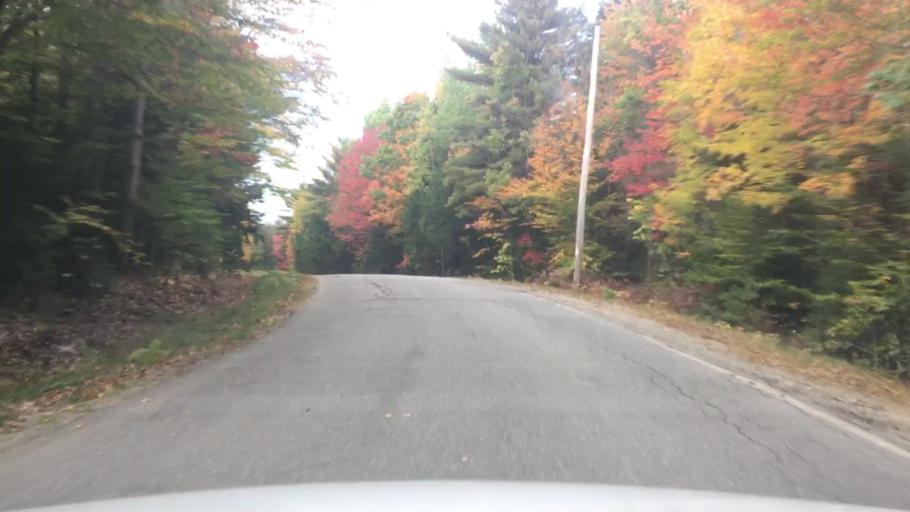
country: US
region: Maine
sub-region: Knox County
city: Washington
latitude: 44.3277
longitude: -69.3665
